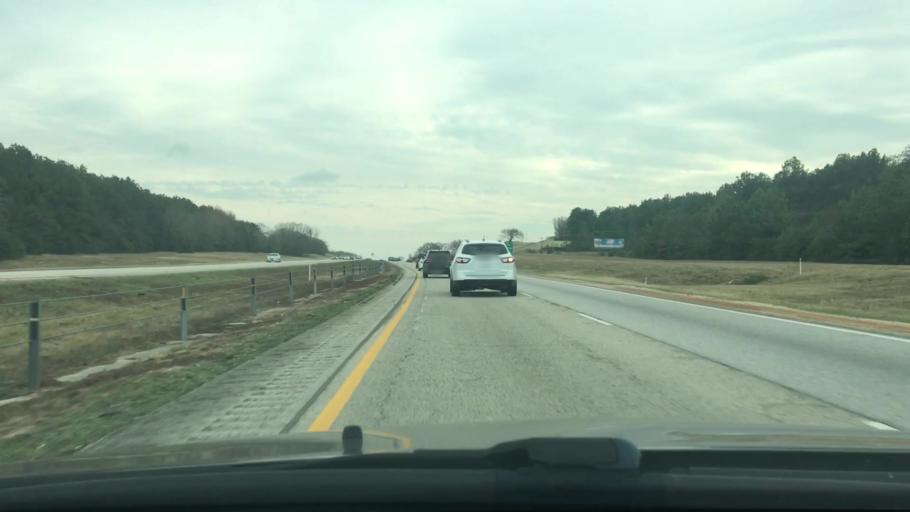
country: US
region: Texas
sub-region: Leon County
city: Centerville
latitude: 31.2937
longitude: -95.9979
